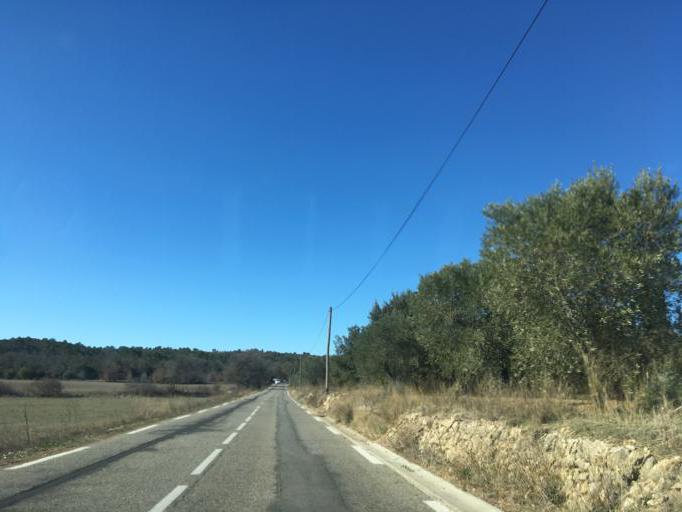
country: FR
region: Provence-Alpes-Cote d'Azur
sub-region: Departement du Var
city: Barjols
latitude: 43.5957
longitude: 5.9956
